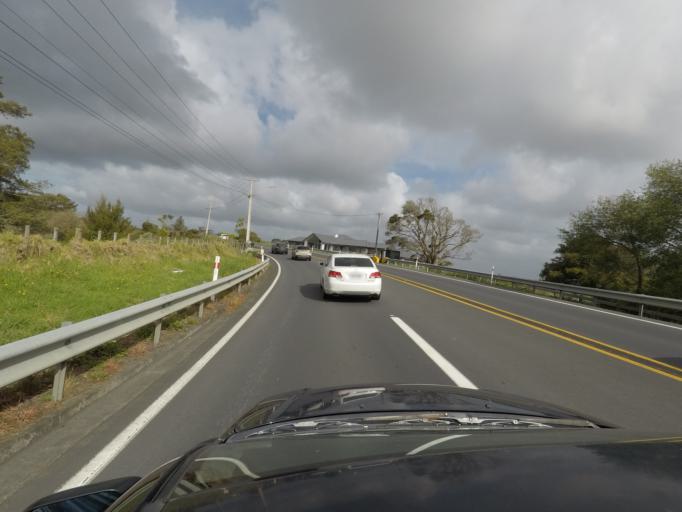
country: NZ
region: Auckland
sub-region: Auckland
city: Pakuranga
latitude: -36.9425
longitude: 174.9465
